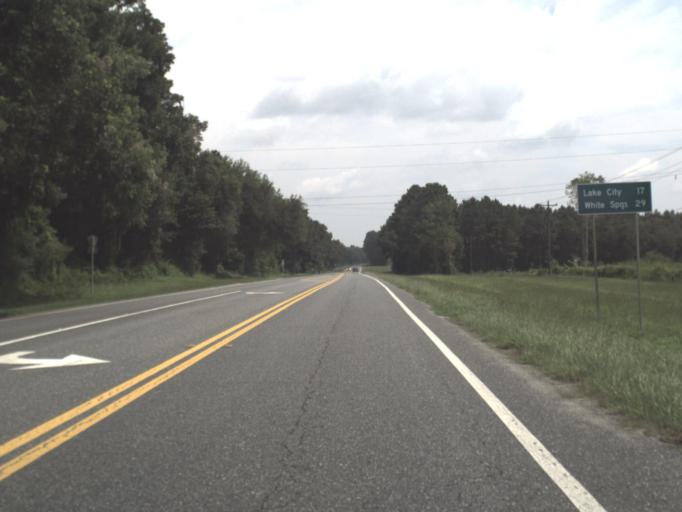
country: US
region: Florida
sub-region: Alachua County
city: High Springs
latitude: 29.9529
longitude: -82.6051
